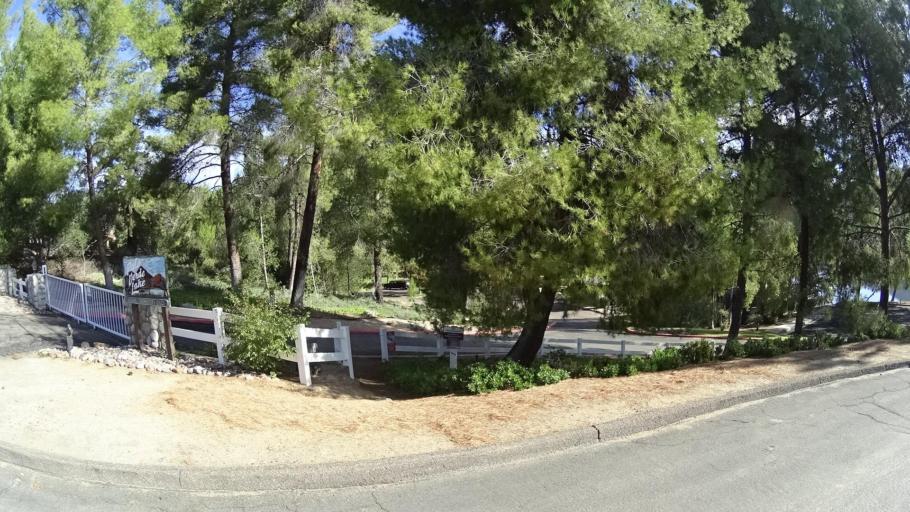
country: US
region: California
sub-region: San Diego County
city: Alpine
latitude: 32.8123
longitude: -116.7316
